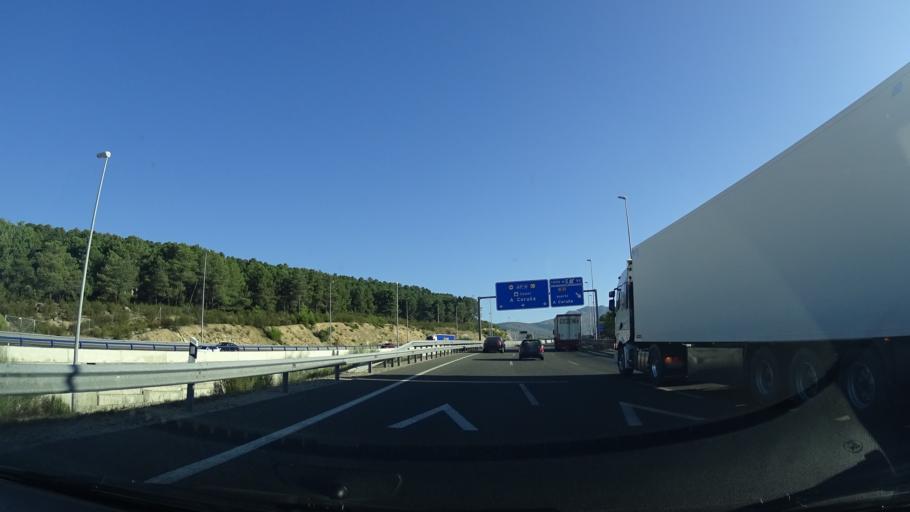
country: ES
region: Madrid
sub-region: Provincia de Madrid
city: Guadarrama
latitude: 40.6804
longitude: -4.1178
